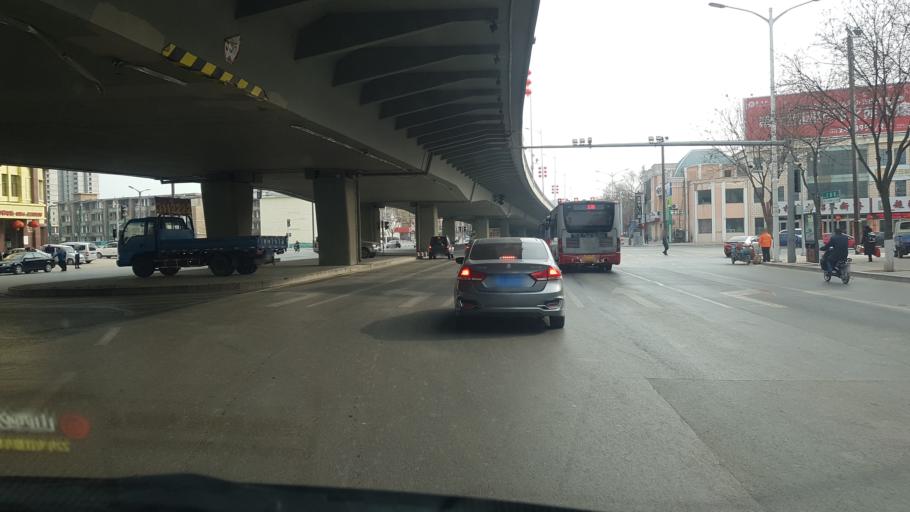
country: CN
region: Shanxi Sheng
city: Yuci
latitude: 37.6903
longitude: 112.7206
